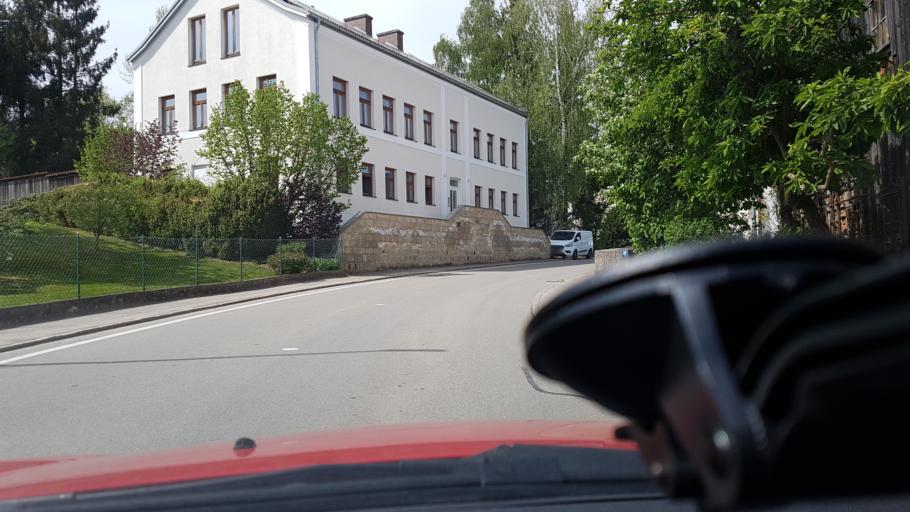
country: DE
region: Bavaria
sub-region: Lower Bavaria
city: Stubenberg
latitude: 48.3397
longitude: 13.0856
